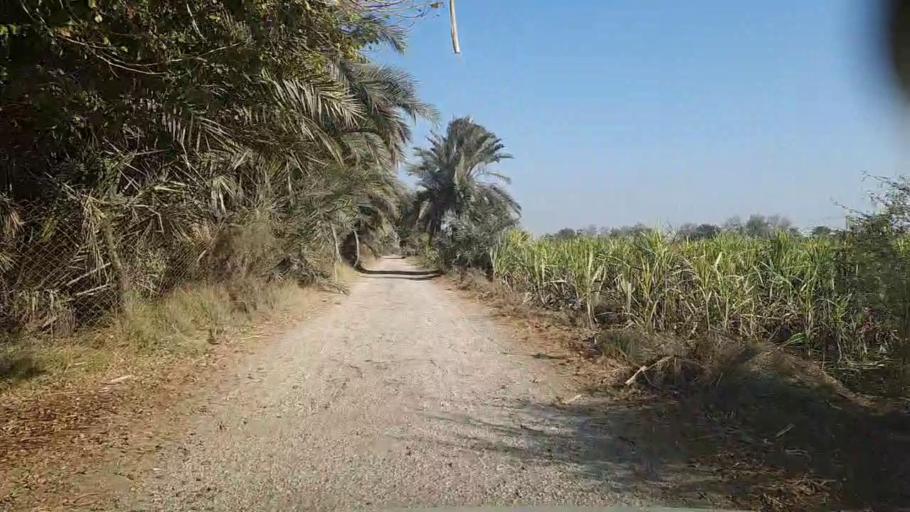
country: PK
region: Sindh
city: Khairpur
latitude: 28.0595
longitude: 69.6907
